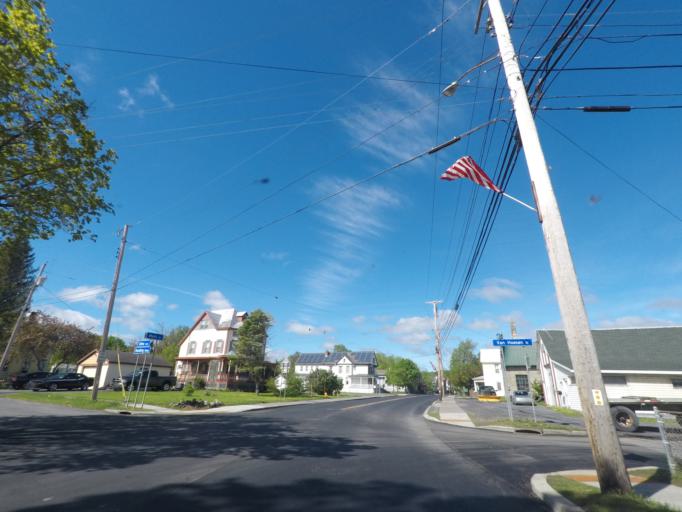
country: US
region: New York
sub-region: Albany County
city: Ravena
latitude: 42.4734
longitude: -73.8009
